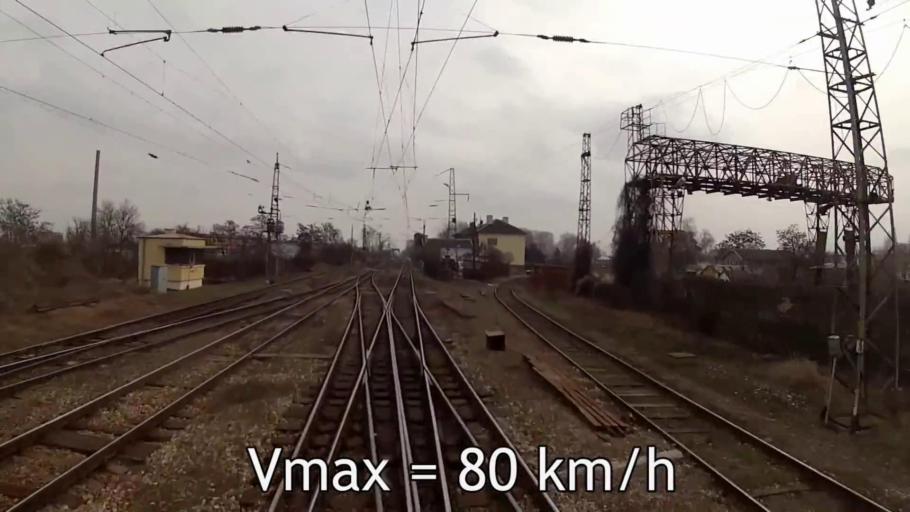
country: BG
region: Sofiya
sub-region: Obshtina Elin Pelin
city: Elin Pelin
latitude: 42.6540
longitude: 23.4614
